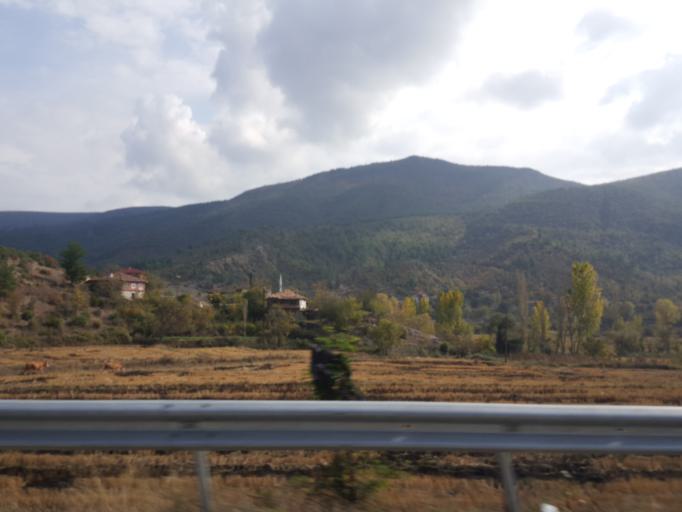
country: TR
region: Sinop
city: Sarayduzu
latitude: 41.3682
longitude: 34.8903
